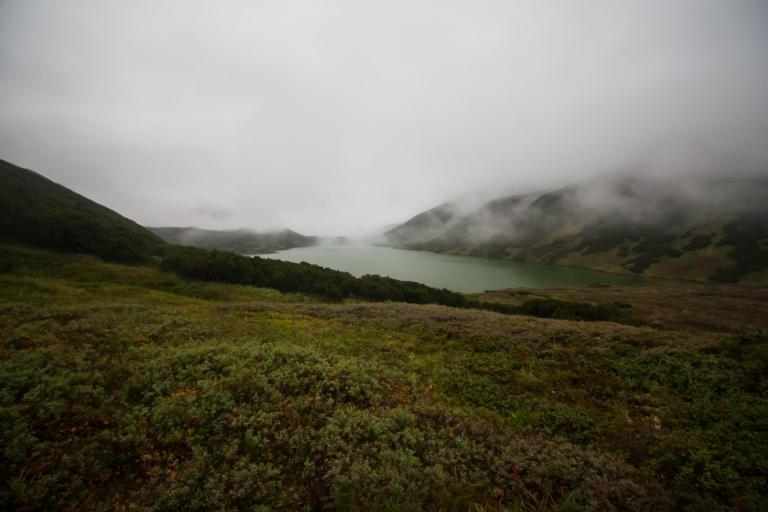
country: RU
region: Kamtsjatka
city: Yelizovo
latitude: 53.9565
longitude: 158.0726
